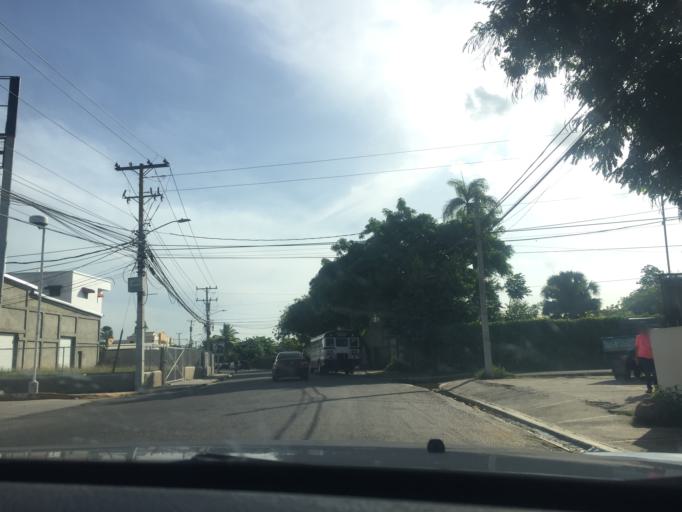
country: DO
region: Santiago
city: Tamboril
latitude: 19.4693
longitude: -70.6532
